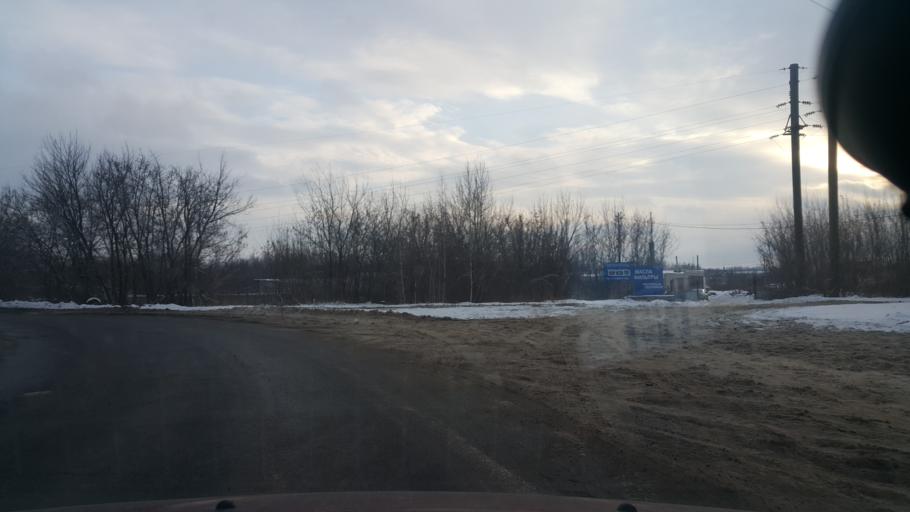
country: RU
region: Tambov
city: Pokrovo-Prigorodnoye
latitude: 52.6553
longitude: 41.4222
